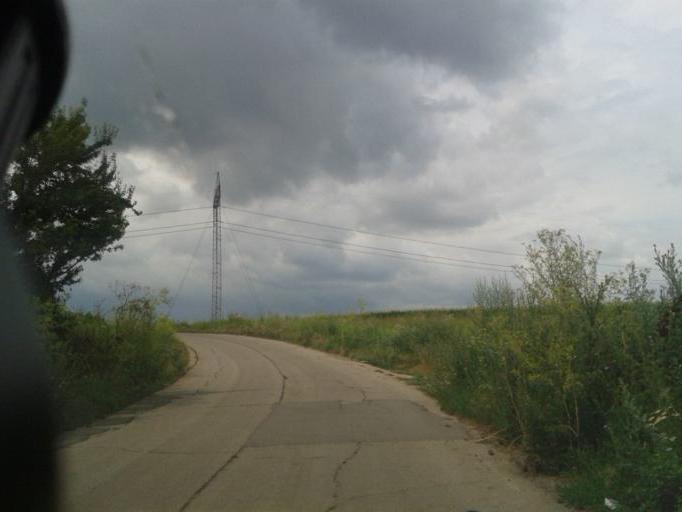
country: RO
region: Calarasi
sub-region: Comuna Fundulea
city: Fundulea
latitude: 44.4900
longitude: 26.5121
